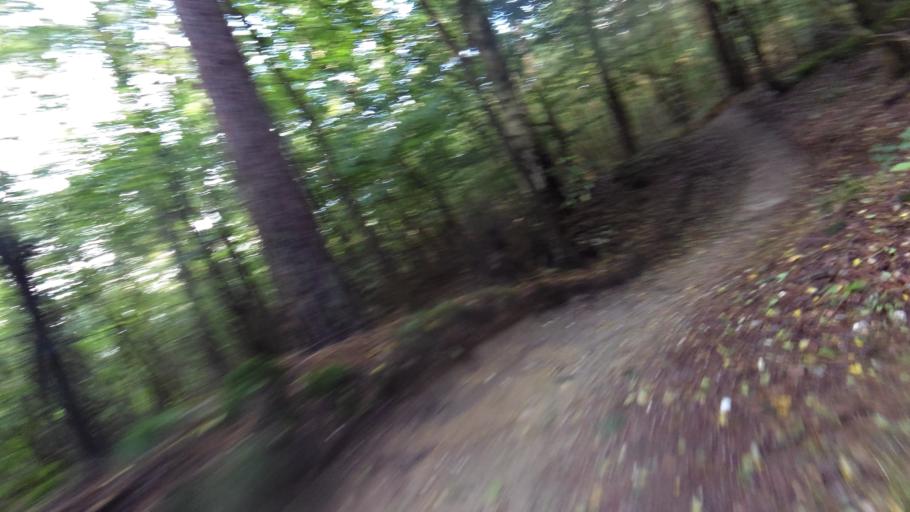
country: NL
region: Utrecht
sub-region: Gemeente Utrechtse Heuvelrug
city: Overberg
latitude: 52.0231
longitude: 5.4775
